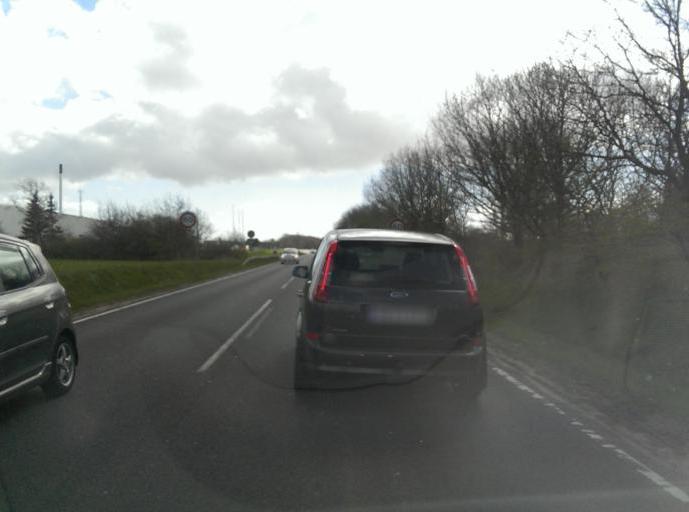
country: DK
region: South Denmark
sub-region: Esbjerg Kommune
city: Esbjerg
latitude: 55.5082
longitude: 8.4056
